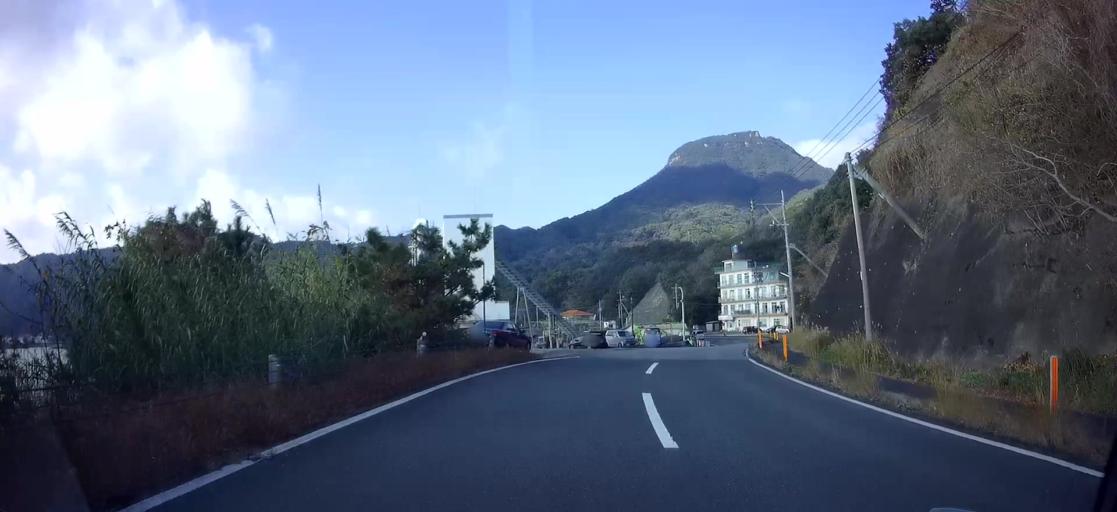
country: JP
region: Kumamoto
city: Minamata
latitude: 32.3871
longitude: 130.3778
